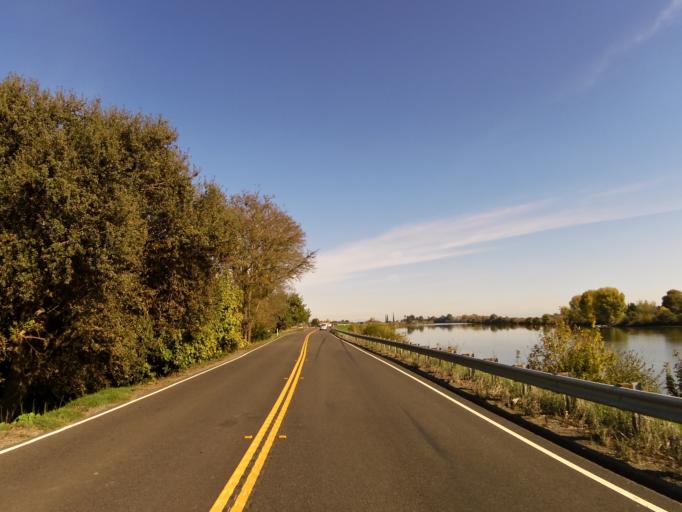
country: US
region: California
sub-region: Sacramento County
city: Walnut Grove
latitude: 38.1882
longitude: -121.5817
